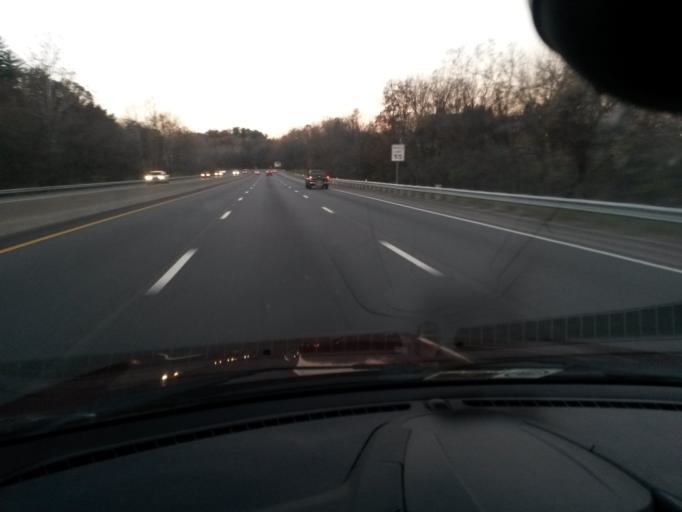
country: US
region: Virginia
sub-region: City of Roanoke
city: Roanoke
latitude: 37.2463
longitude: -79.9676
